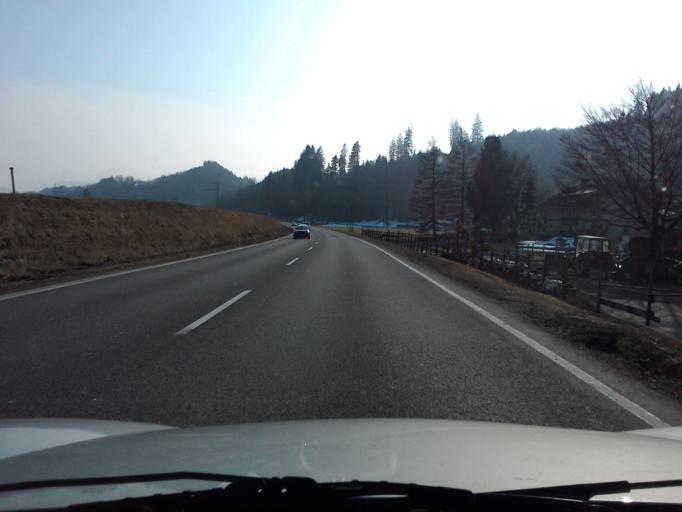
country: DE
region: Bavaria
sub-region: Swabia
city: Sonthofen
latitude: 47.5035
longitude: 10.2685
